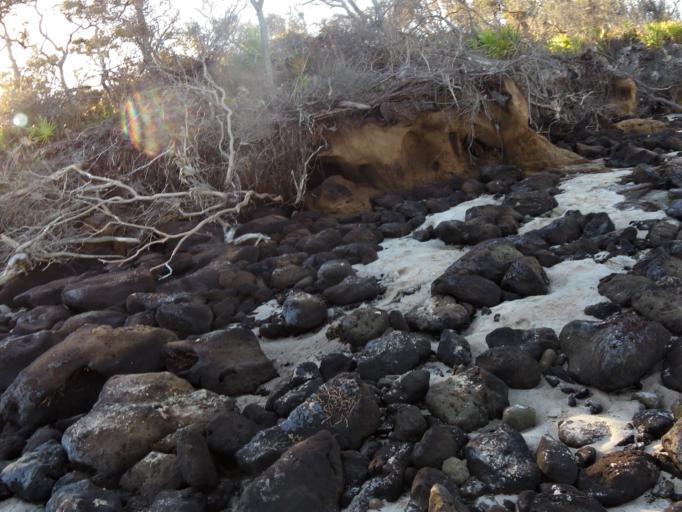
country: US
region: Florida
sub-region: Duval County
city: Atlantic Beach
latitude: 30.4931
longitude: -81.4375
